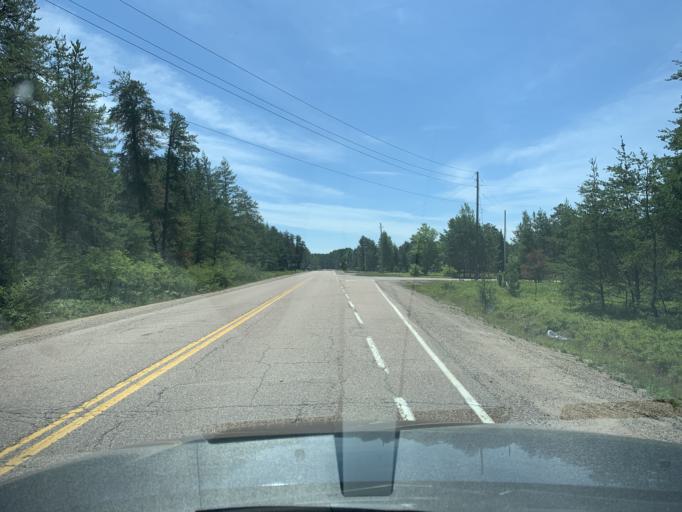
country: CA
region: Ontario
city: Petawawa
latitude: 45.6598
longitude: -77.5802
